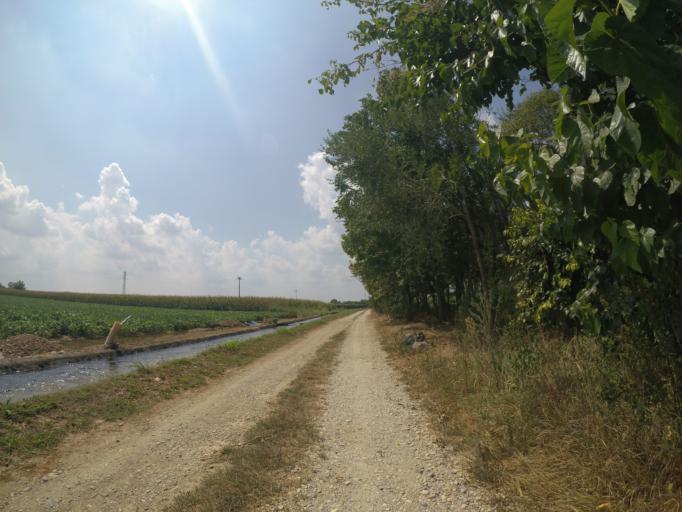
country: IT
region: Friuli Venezia Giulia
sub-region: Provincia di Udine
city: Bertiolo
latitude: 45.9513
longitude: 13.0335
